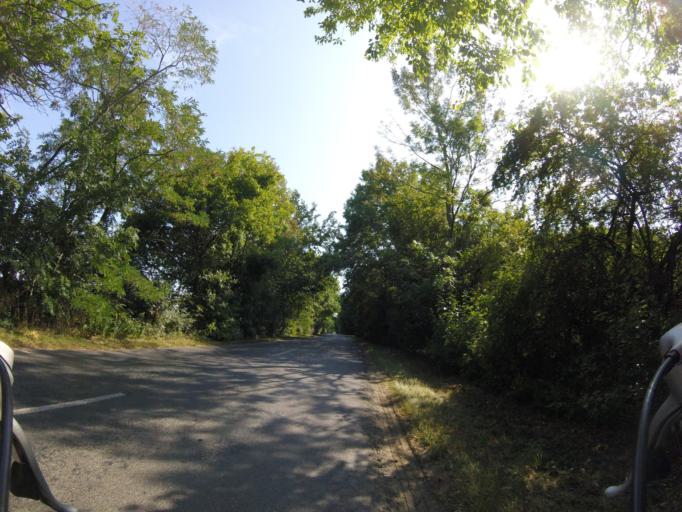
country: HU
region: Komarom-Esztergom
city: Bajna
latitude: 47.6741
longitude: 18.5743
